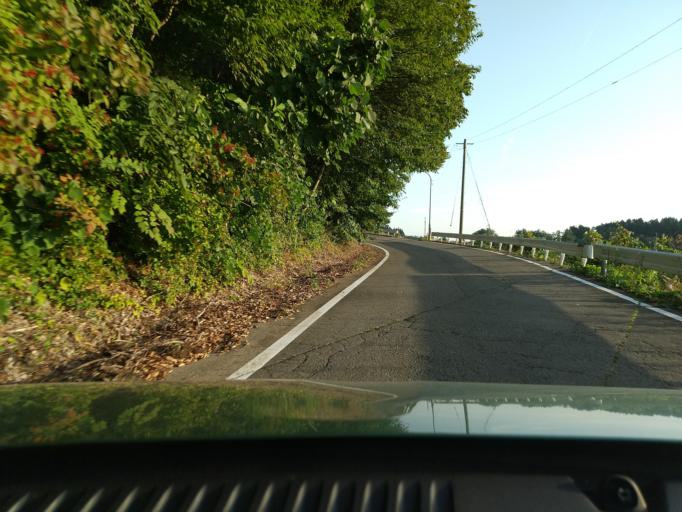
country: JP
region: Akita
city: Omagari
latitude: 39.4209
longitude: 140.5854
